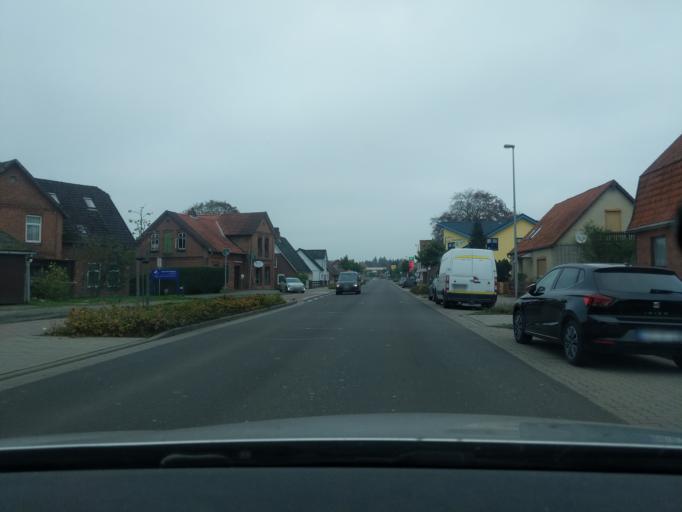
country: DE
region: Lower Saxony
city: Hemmoor
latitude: 53.6797
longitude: 9.1802
